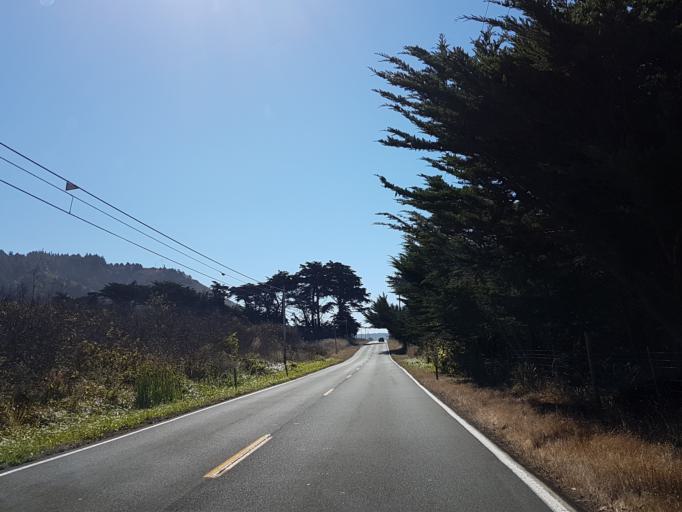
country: US
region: California
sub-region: Mendocino County
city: Boonville
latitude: 39.0897
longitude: -123.7009
